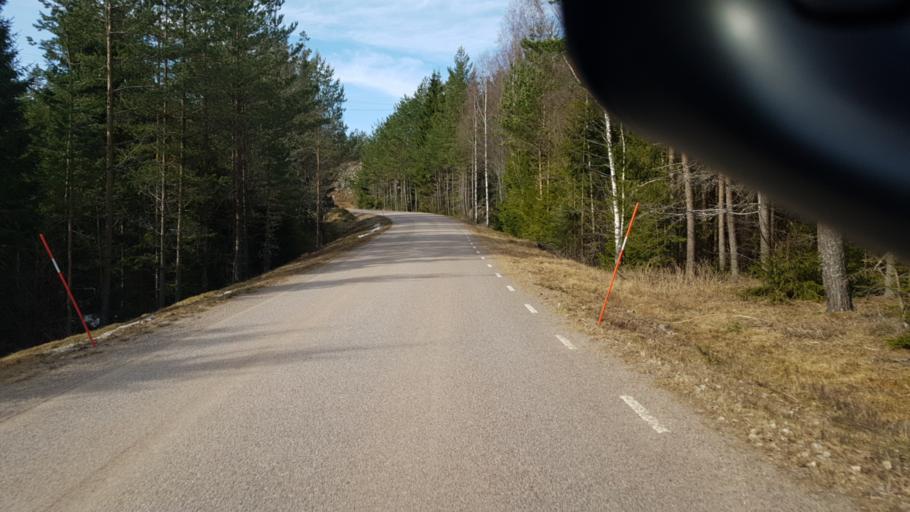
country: SE
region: Vaermland
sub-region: Arvika Kommun
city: Arvika
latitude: 59.5415
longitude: 12.5170
